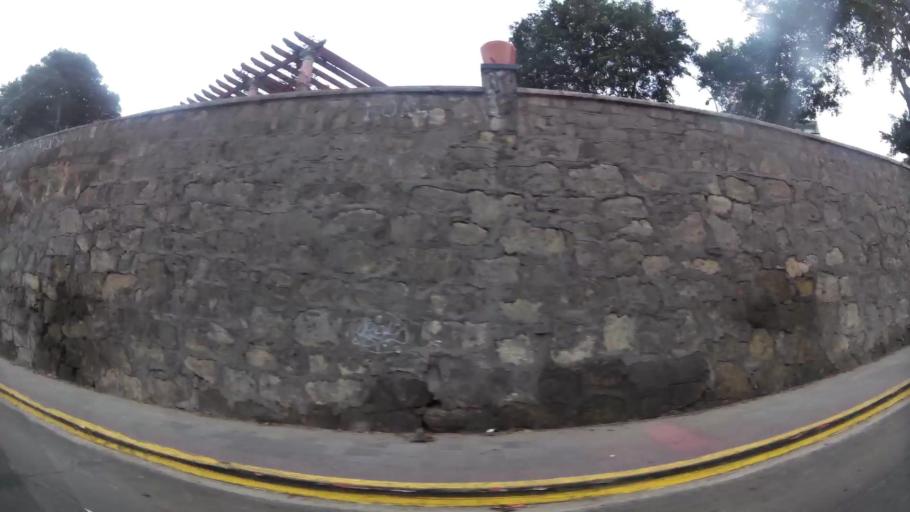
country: PE
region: Lima
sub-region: Lima
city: Surco
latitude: -12.1647
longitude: -77.0255
